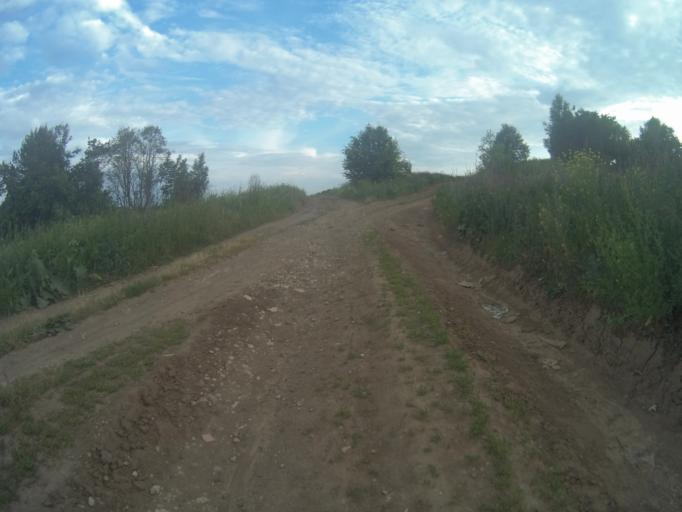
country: RU
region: Vladimir
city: Vladimir
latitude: 56.2136
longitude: 40.3929
